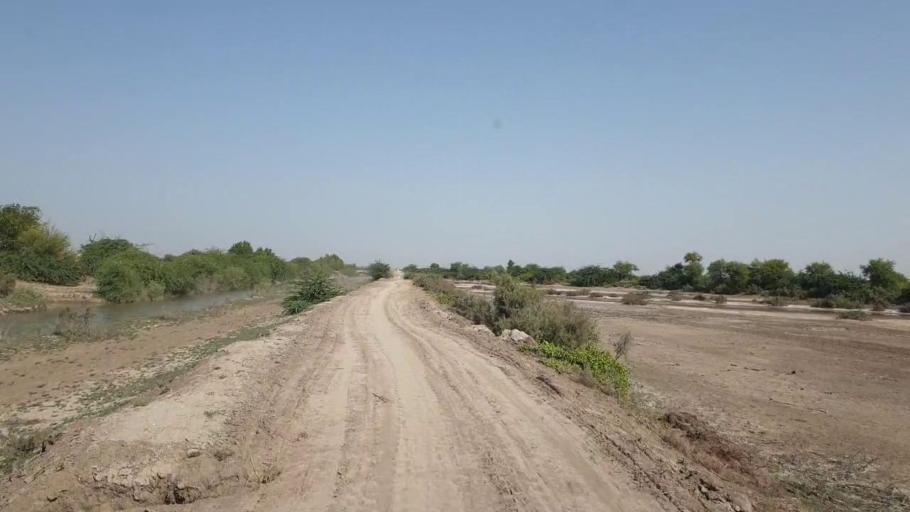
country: PK
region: Sindh
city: Tando Bago
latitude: 24.6659
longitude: 69.0676
